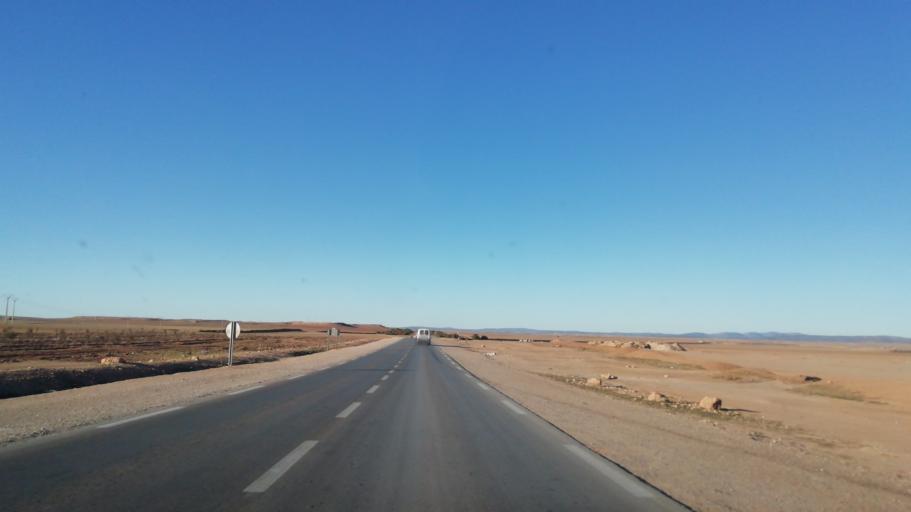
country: DZ
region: Tlemcen
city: Sebdou
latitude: 34.4851
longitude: -1.2722
